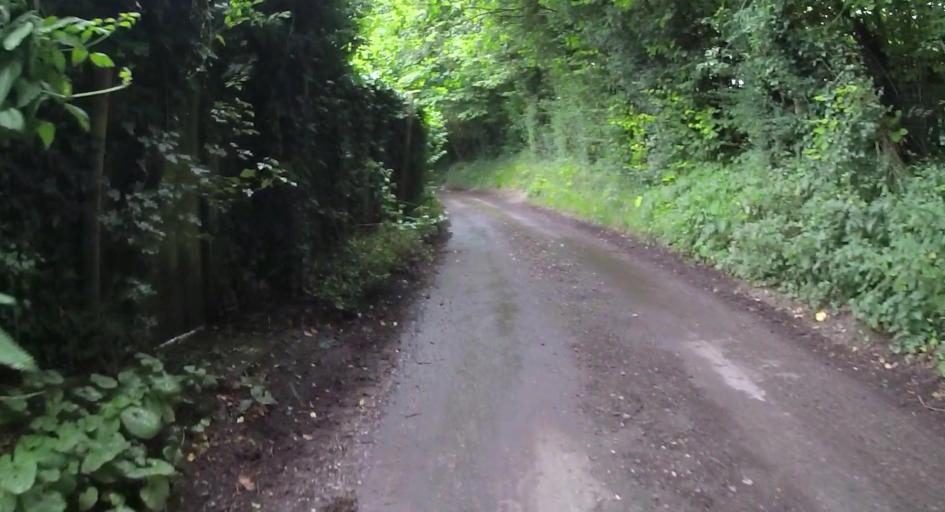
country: GB
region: England
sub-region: Hampshire
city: Highclere
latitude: 51.2568
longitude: -1.4134
